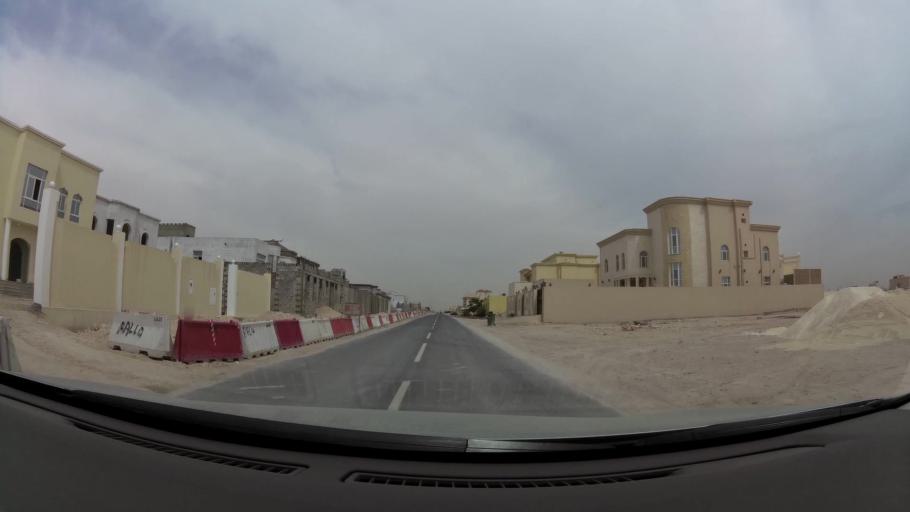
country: QA
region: Baladiyat ar Rayyan
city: Ar Rayyan
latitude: 25.2170
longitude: 51.4640
